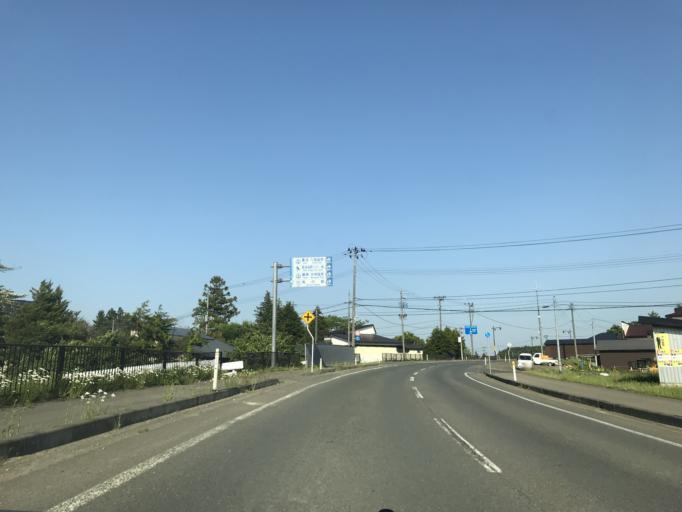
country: JP
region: Iwate
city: Kitakami
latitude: 39.2841
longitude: 141.0473
